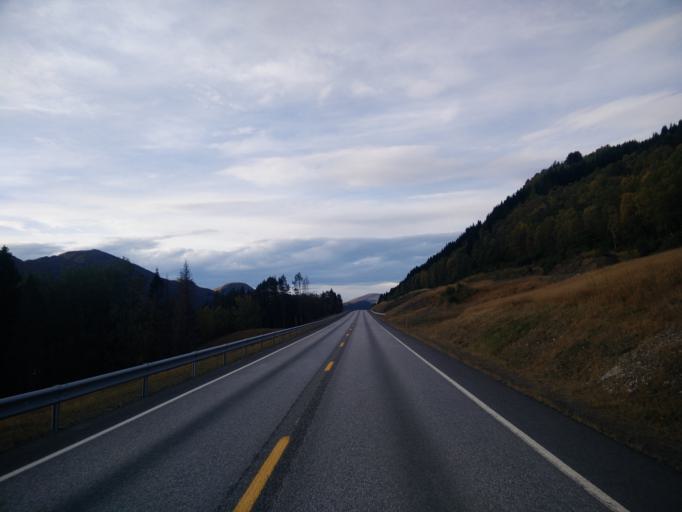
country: NO
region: More og Romsdal
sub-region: Gjemnes
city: Batnfjordsora
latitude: 62.9197
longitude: 7.6981
